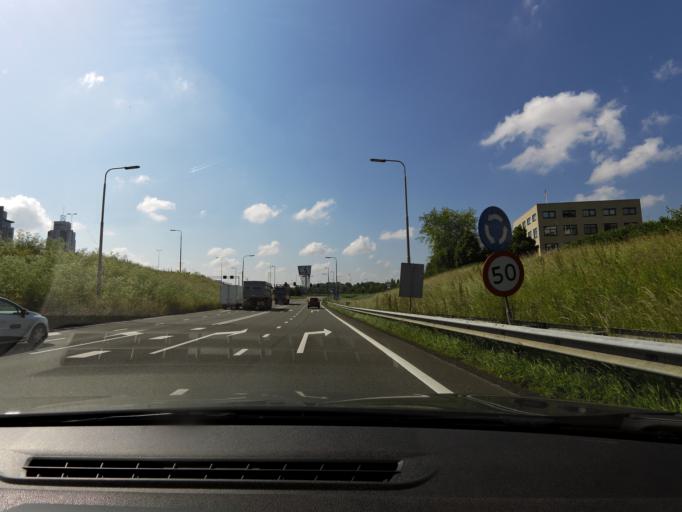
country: NL
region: South Holland
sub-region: Gemeente Rotterdam
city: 's-Gravenland
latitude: 51.9166
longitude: 4.5338
